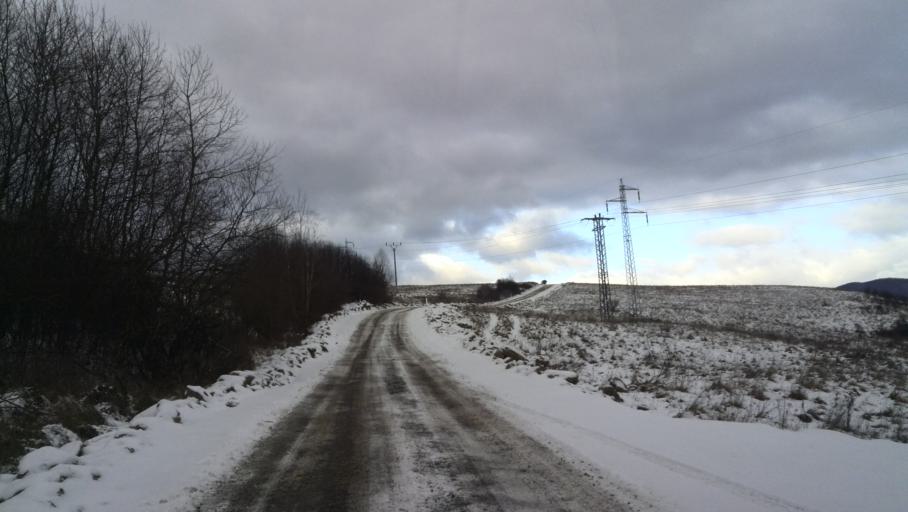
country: SK
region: Kosicky
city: Gelnica
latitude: 48.8197
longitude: 21.0741
